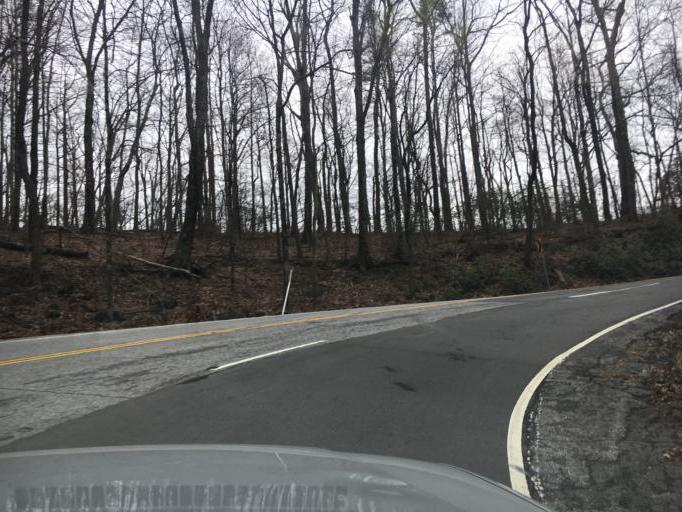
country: US
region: South Carolina
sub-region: Greenville County
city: Slater-Marietta
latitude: 35.1056
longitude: -82.6097
